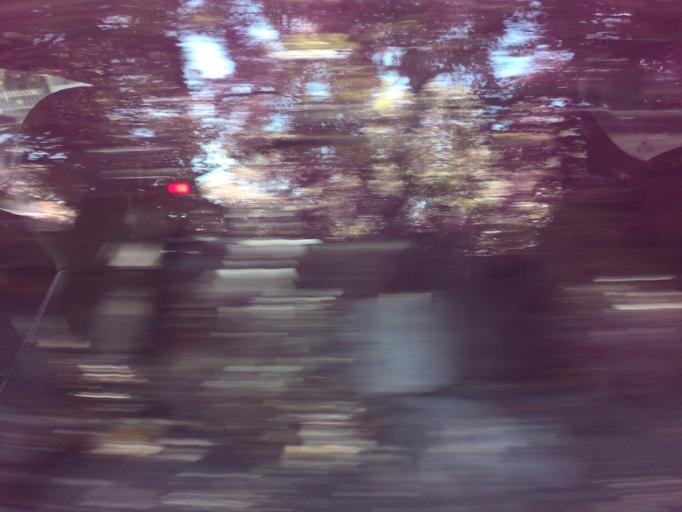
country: PH
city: Sambayanihan People's Village
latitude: 14.4896
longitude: 121.0323
